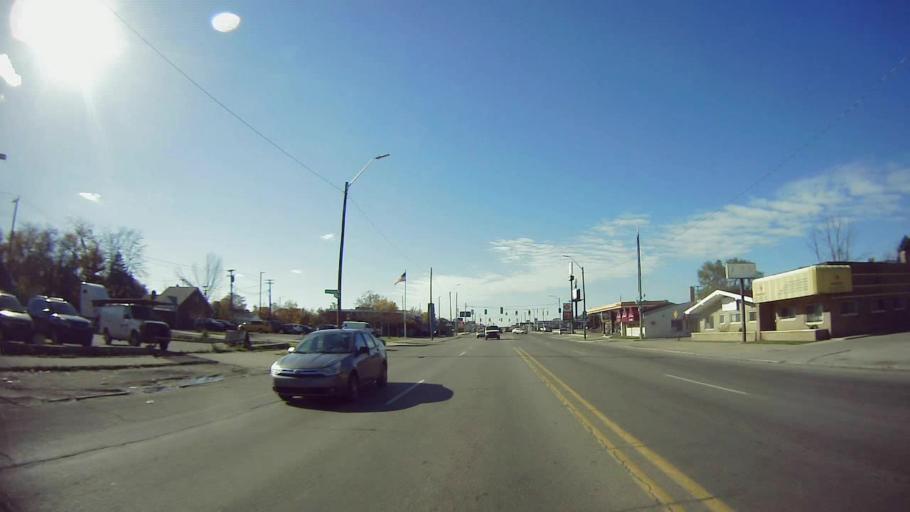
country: US
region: Michigan
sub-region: Wayne County
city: Dearborn
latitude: 42.3433
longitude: -83.2143
